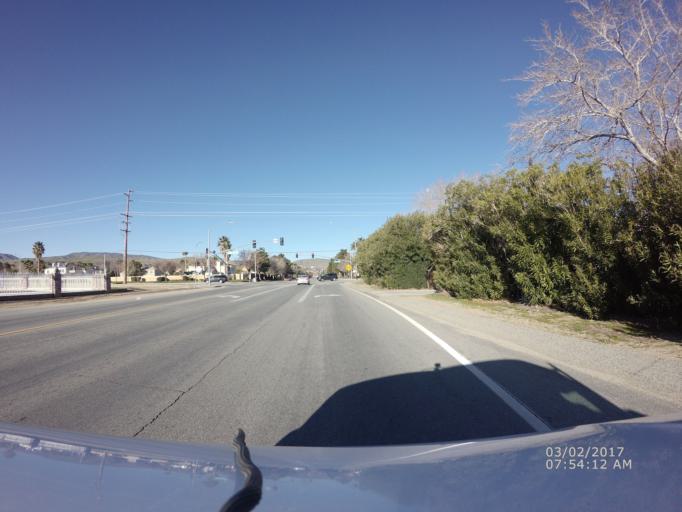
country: US
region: California
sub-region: Los Angeles County
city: Desert View Highlands
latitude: 34.6165
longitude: -118.1830
